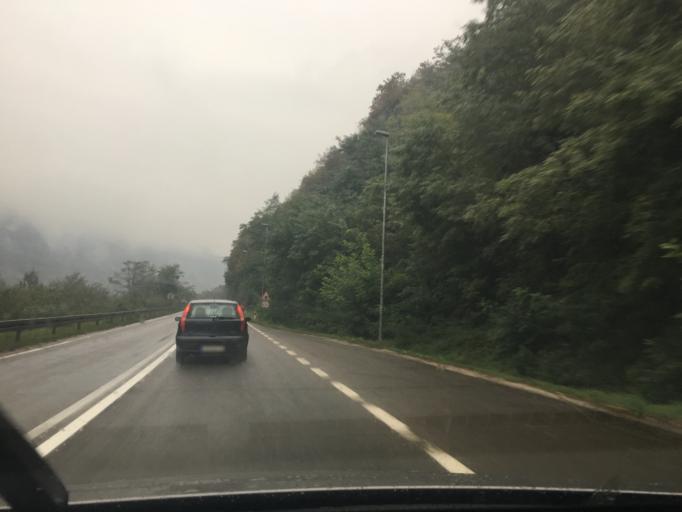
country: RS
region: Central Serbia
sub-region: Pcinjski Okrug
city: Vladicin Han
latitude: 42.7449
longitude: 22.0643
